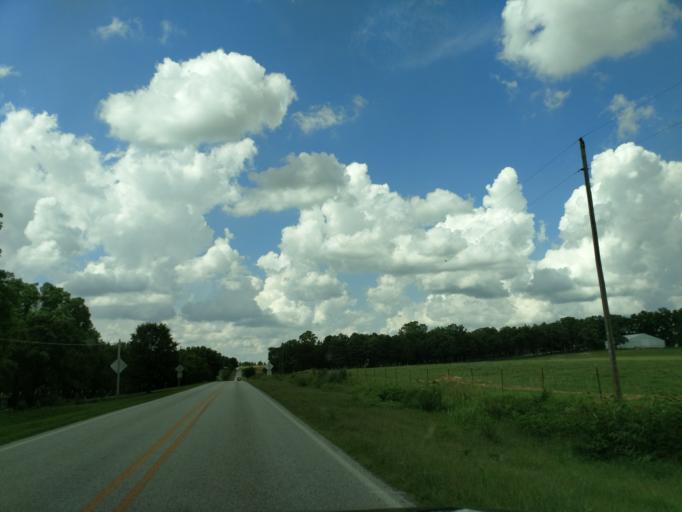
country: US
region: Arkansas
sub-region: Carroll County
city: Berryville
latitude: 36.4220
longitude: -93.5565
